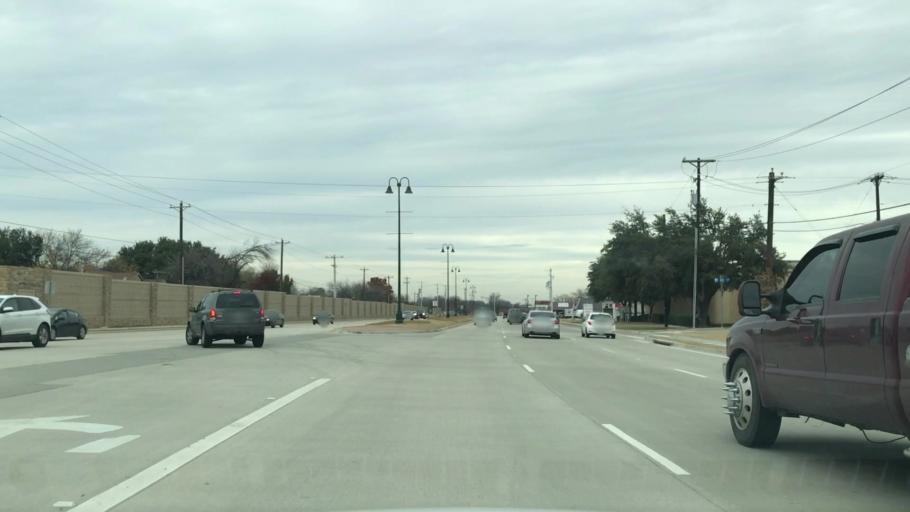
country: US
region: Texas
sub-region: Denton County
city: The Colony
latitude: 33.0987
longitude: -96.8925
